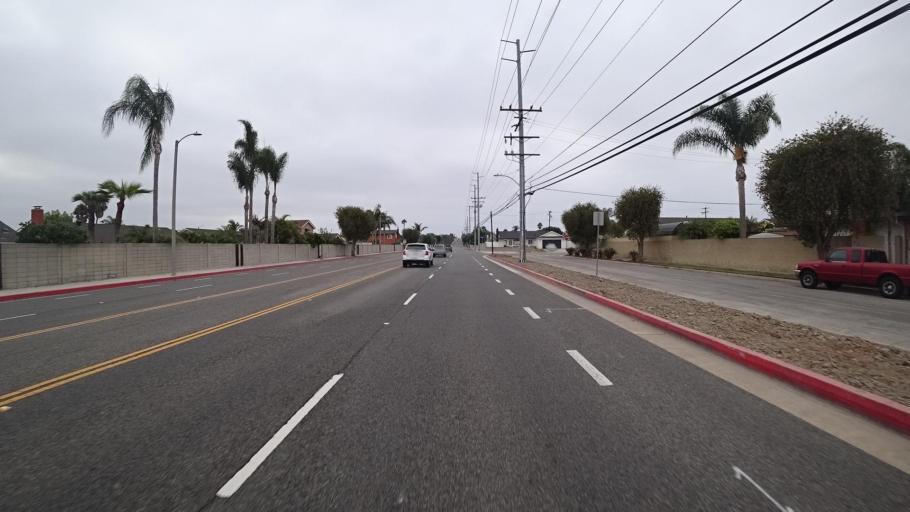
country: US
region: California
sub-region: Orange County
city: Huntington Beach
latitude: 33.7039
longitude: -118.0152
